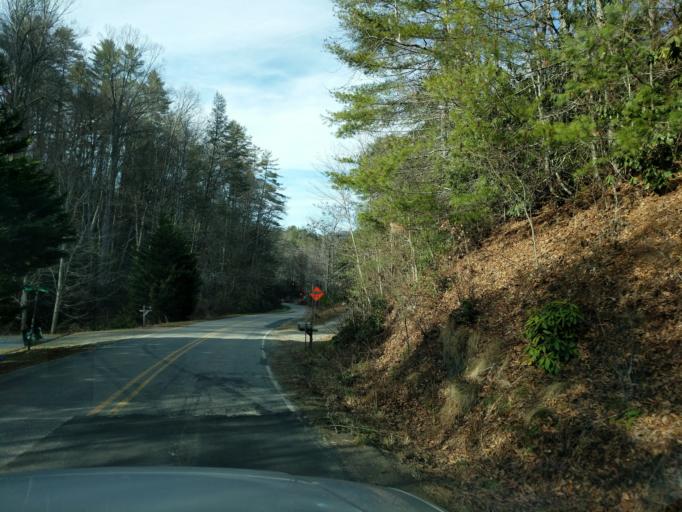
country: US
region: North Carolina
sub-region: Haywood County
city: Cove Creek
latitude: 35.6634
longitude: -83.0122
